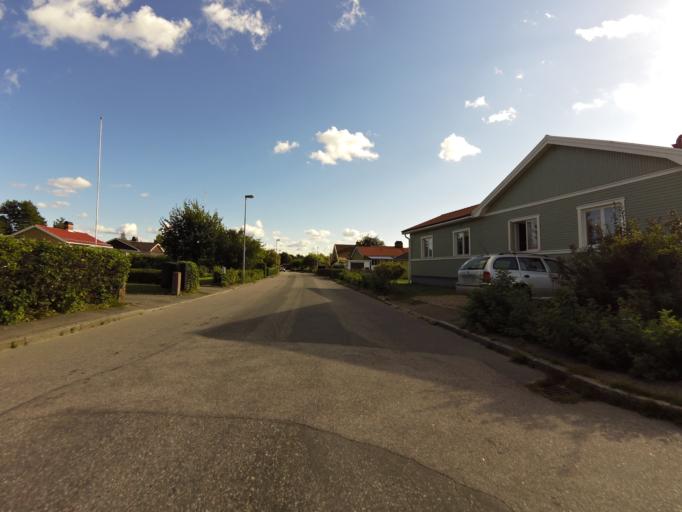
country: SE
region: Gaevleborg
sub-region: Gavle Kommun
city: Gavle
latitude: 60.7030
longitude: 17.1669
